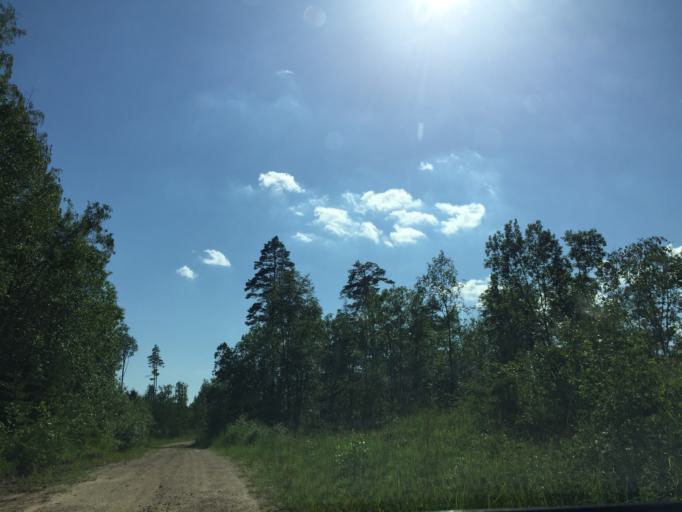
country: LV
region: Tukuma Rajons
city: Tukums
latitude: 57.0203
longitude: 23.2321
